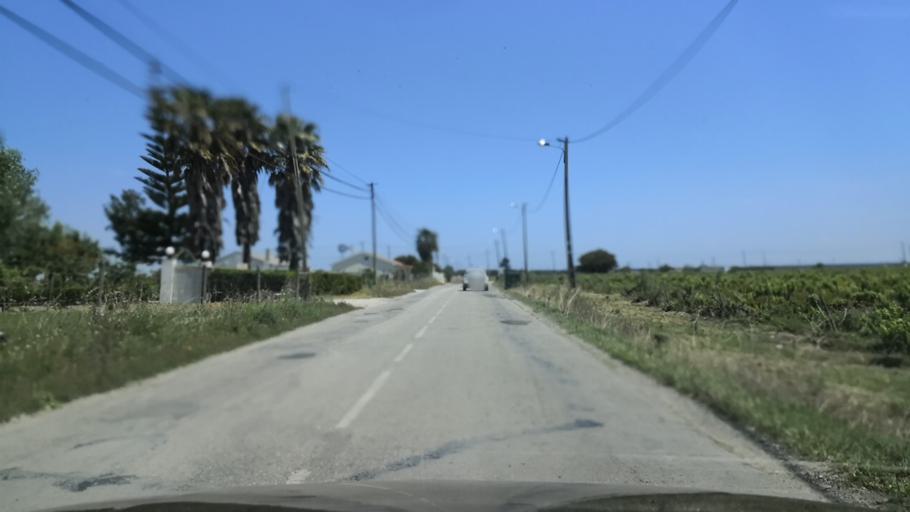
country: PT
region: Setubal
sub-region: Palmela
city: Palmela
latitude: 38.6009
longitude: -8.7979
